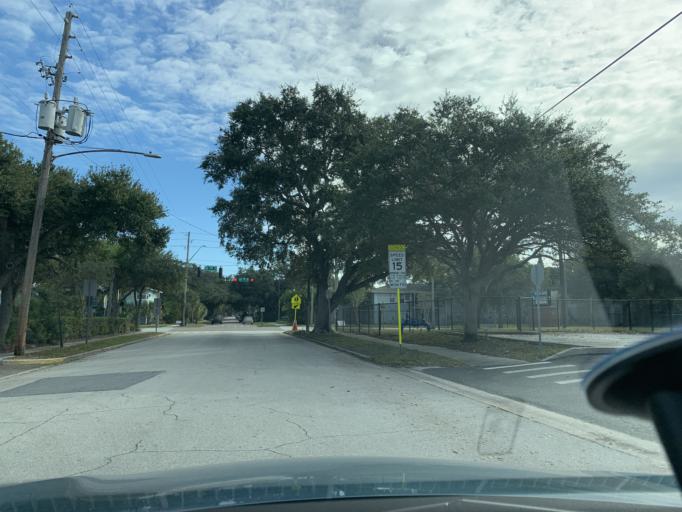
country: US
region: Florida
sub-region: Pinellas County
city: Saint Petersburg
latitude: 27.7884
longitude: -82.6556
